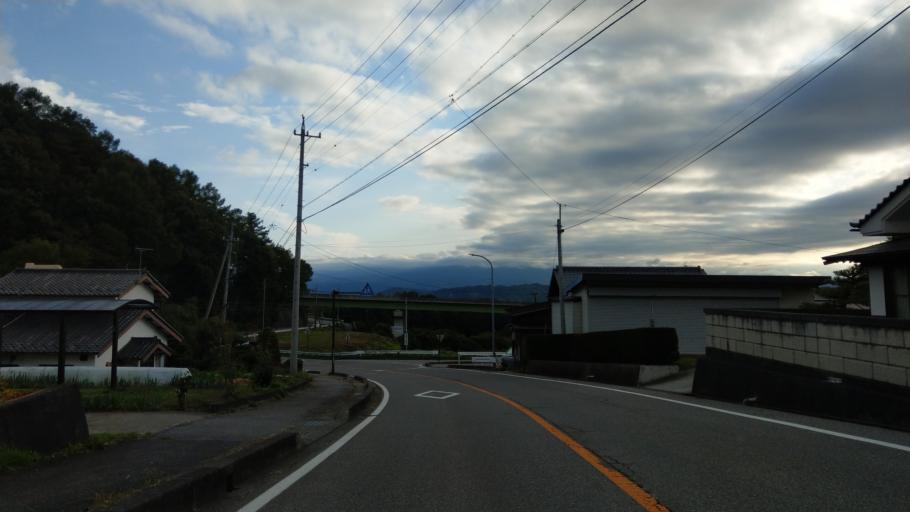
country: JP
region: Nagano
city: Komoro
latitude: 36.3455
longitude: 138.4289
